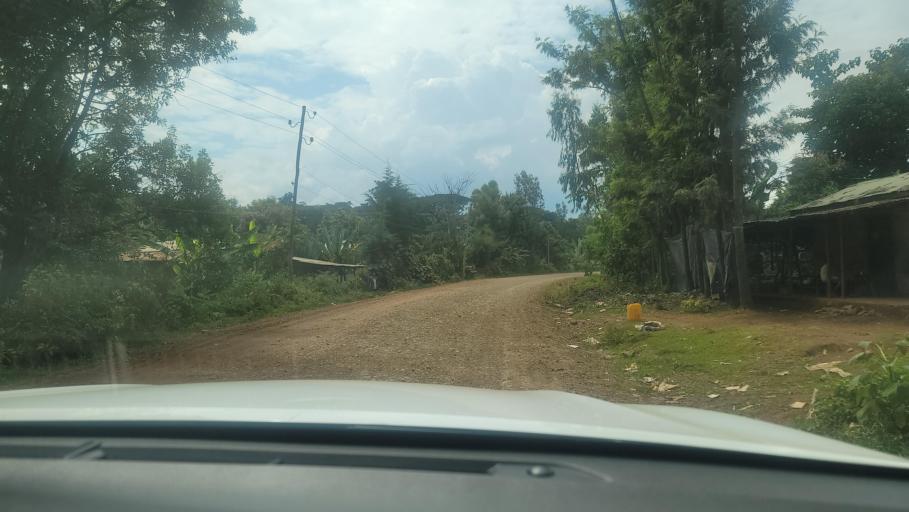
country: ET
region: Oromiya
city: Agaro
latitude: 7.8337
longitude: 36.5431
